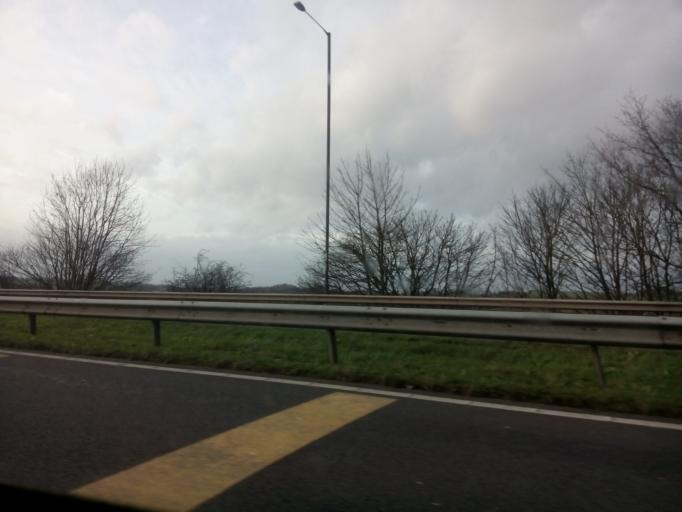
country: GB
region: England
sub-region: Worcestershire
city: Barnt Green
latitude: 52.3806
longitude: -2.0416
